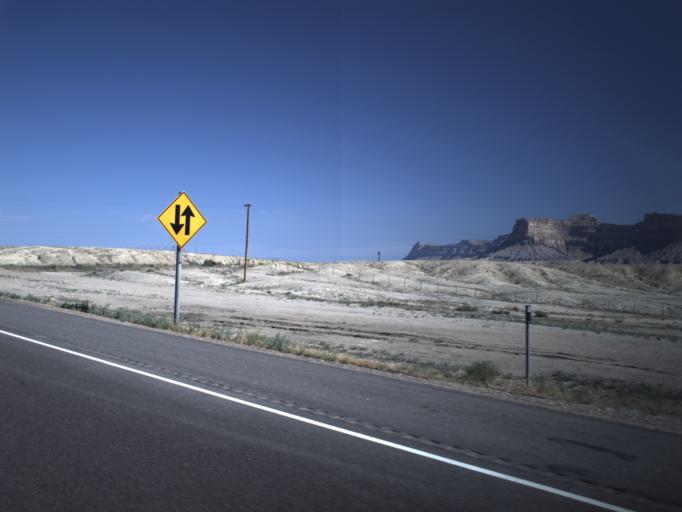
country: US
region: Utah
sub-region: Carbon County
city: East Carbon City
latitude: 38.9879
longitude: -110.2436
